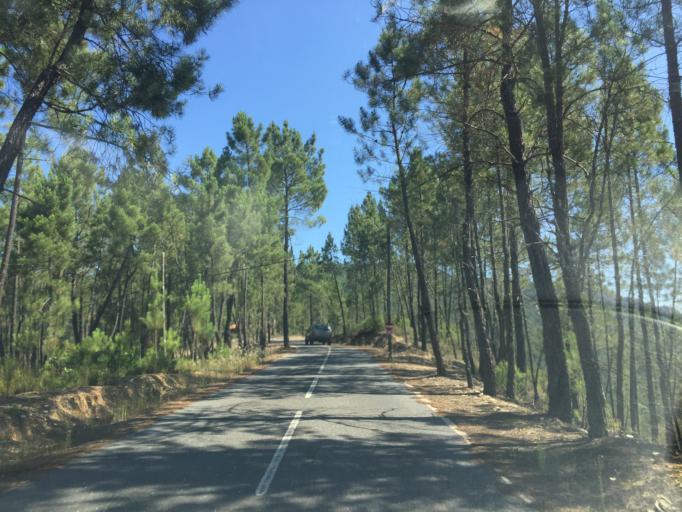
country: PT
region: Coimbra
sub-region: Pampilhosa da Serra
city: Pampilhosa da Serra
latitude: 40.0290
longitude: -7.8234
